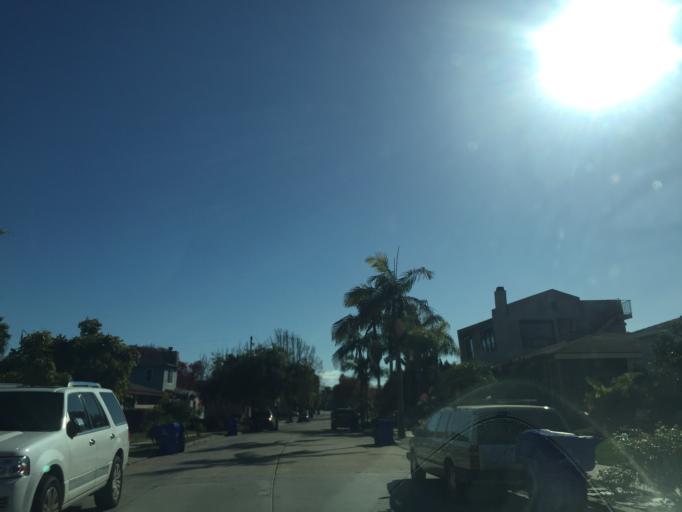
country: US
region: California
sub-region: San Diego County
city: La Jolla
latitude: 32.7855
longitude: -117.2374
